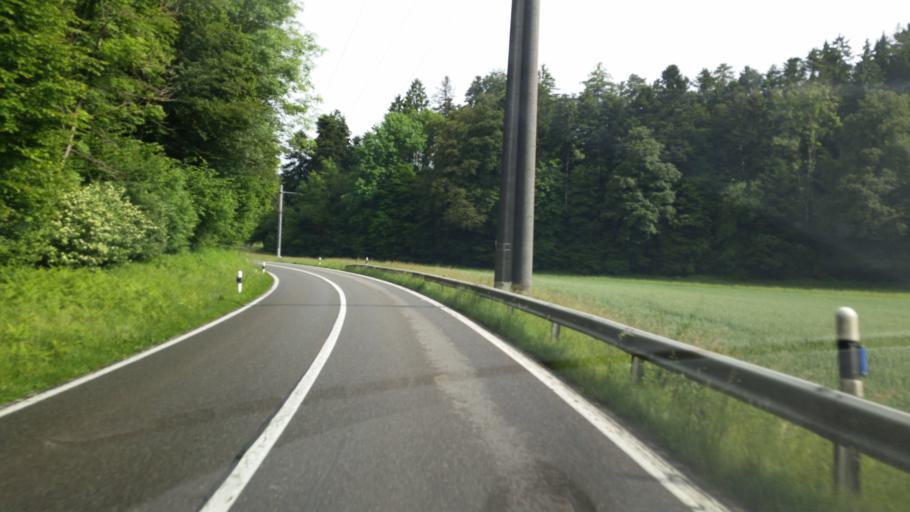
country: CH
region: Aargau
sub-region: Bezirk Bremgarten
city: Bremgarten
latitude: 47.3233
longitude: 8.3486
